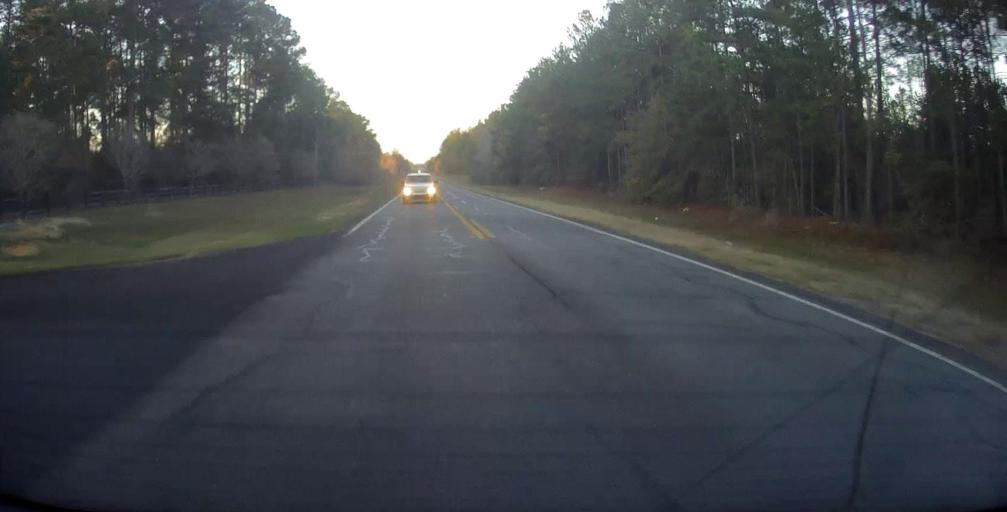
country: US
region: Georgia
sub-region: Dodge County
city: Eastman
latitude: 32.2319
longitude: -83.1513
